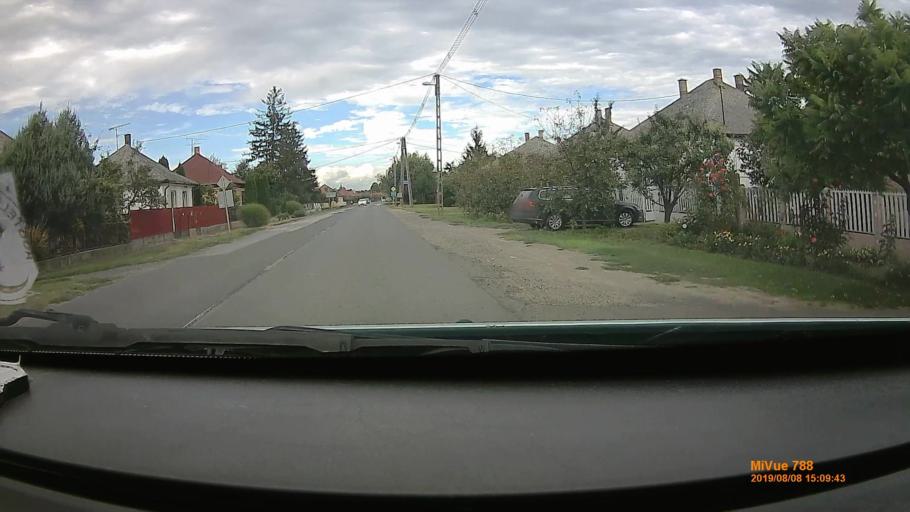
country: HU
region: Szabolcs-Szatmar-Bereg
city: Tunyogmatolcs
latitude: 47.9663
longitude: 22.4487
